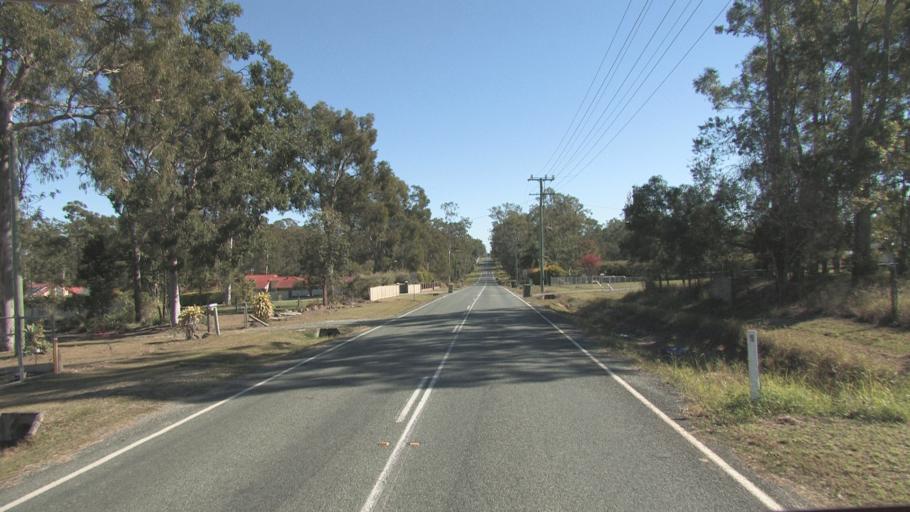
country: AU
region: Queensland
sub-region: Logan
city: Park Ridge South
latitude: -27.7287
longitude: 153.0523
